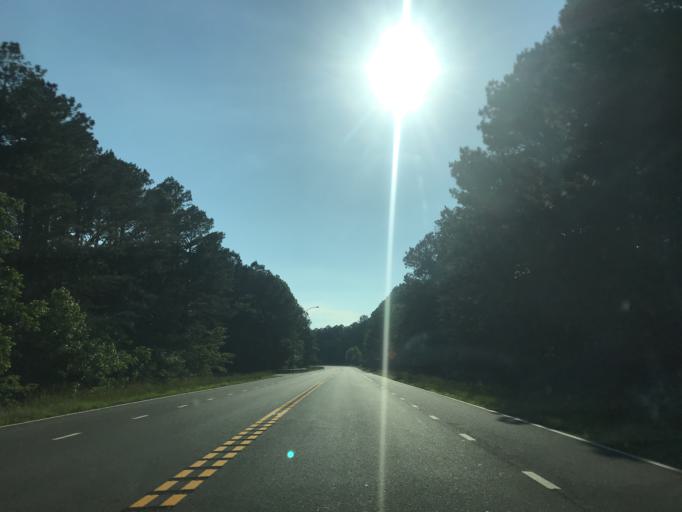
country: US
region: Maryland
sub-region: Wicomico County
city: Hebron
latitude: 38.5333
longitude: -75.7241
